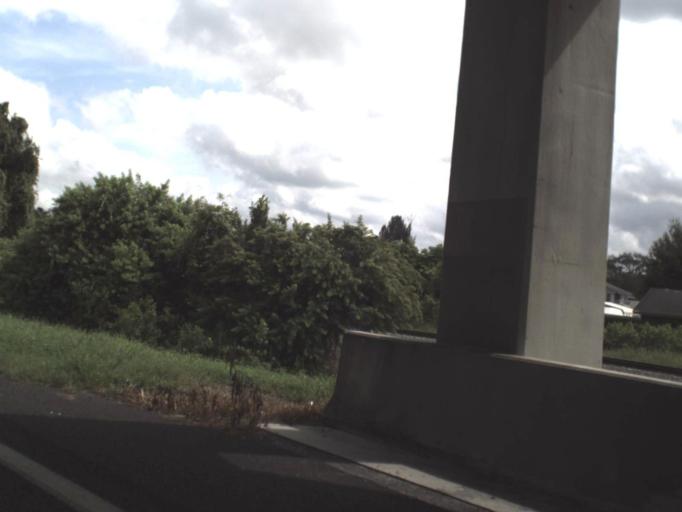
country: US
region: Florida
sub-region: Manatee County
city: Memphis
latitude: 27.5398
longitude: -82.5638
